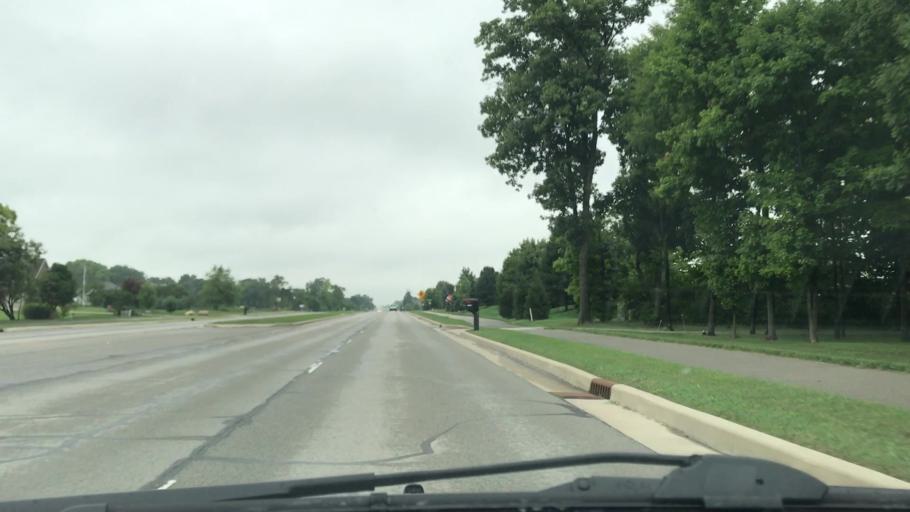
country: US
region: Indiana
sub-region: Hamilton County
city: Westfield
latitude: 40.0252
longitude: -86.0706
